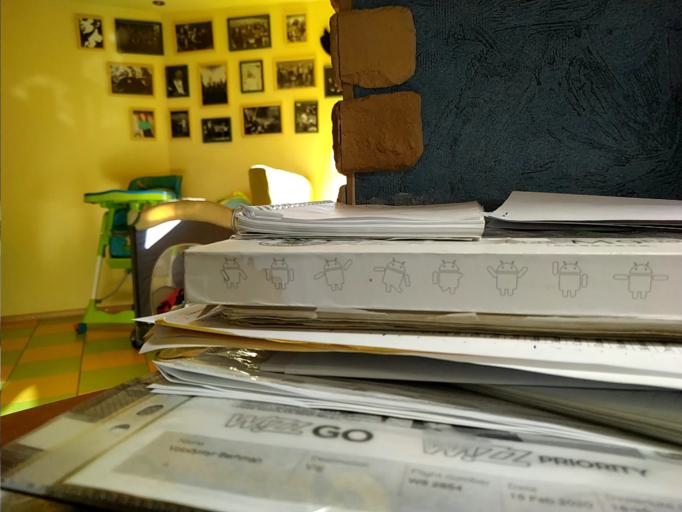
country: RU
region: Novgorod
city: Volot
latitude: 57.6127
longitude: 30.7890
